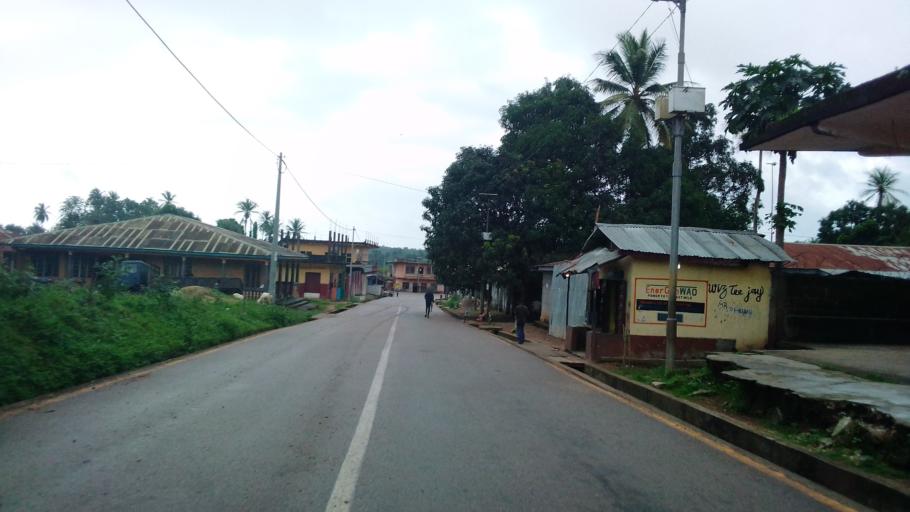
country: SL
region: Northern Province
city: Lunsar
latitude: 8.6811
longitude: -12.5327
